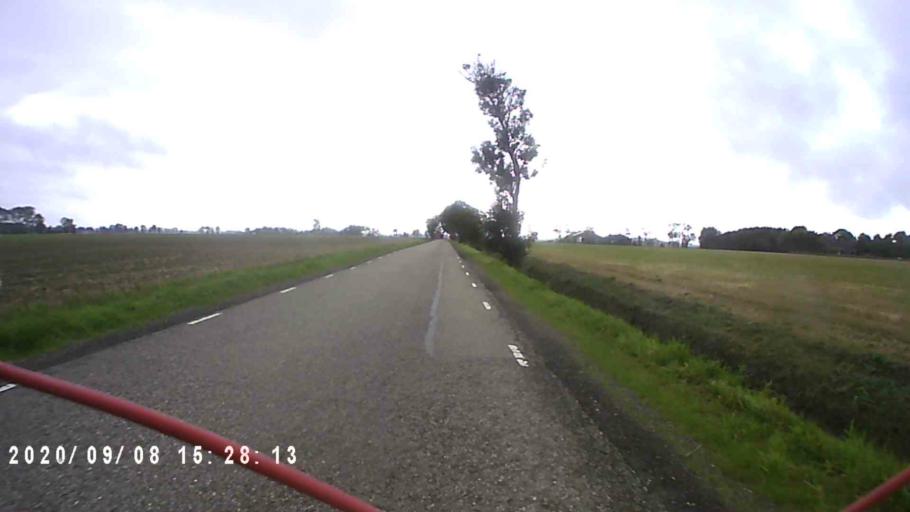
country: NL
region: Groningen
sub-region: Gemeente Bedum
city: Bedum
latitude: 53.2945
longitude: 6.6568
